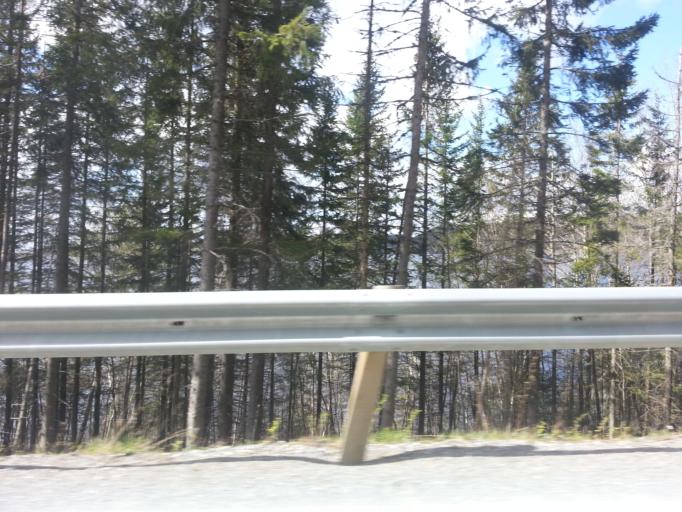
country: NO
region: Nord-Trondelag
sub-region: Levanger
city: Skogn
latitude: 63.6205
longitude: 11.1590
